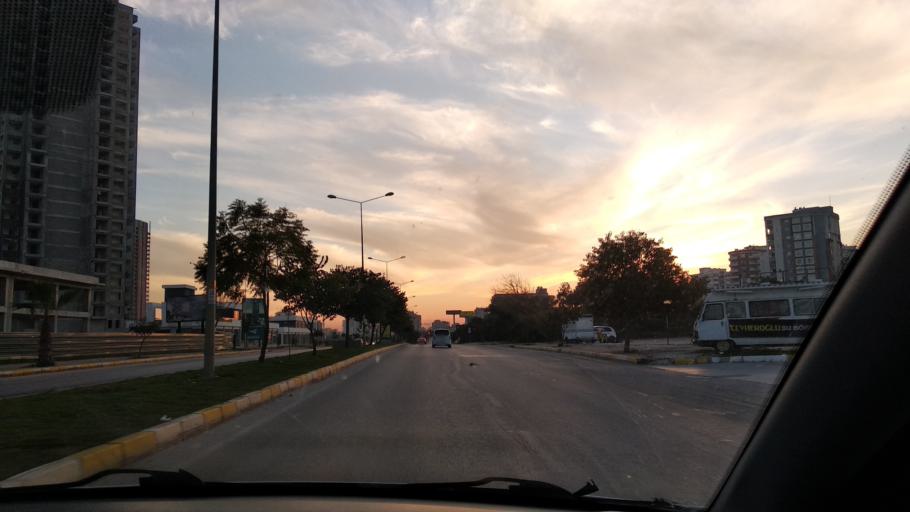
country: TR
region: Mersin
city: Mercin
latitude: 36.7996
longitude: 34.5809
